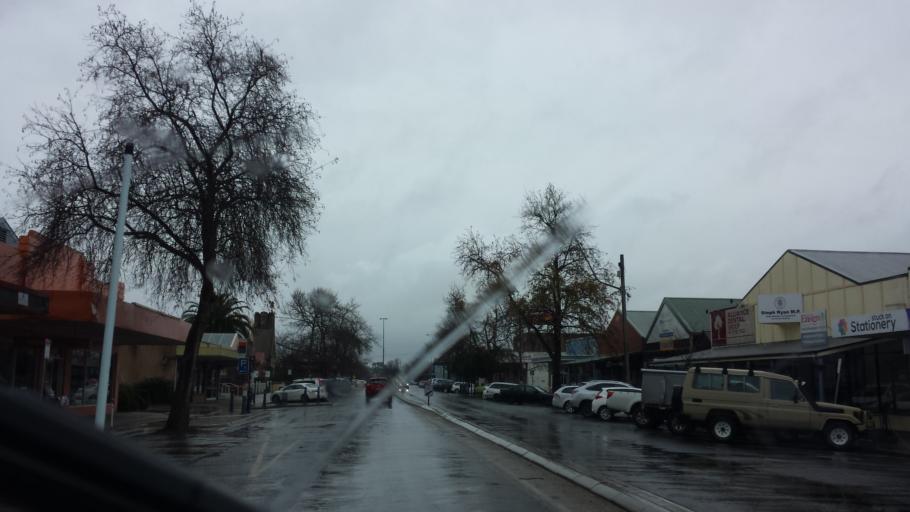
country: AU
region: Victoria
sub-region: Benalla
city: Benalla
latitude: -36.5510
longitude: 145.9856
